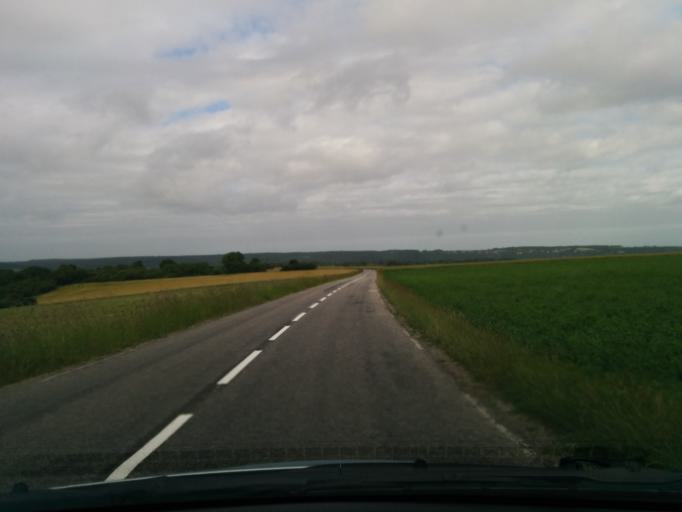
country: FR
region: Ile-de-France
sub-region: Departement des Yvelines
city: Buchelay
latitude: 49.0138
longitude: 1.6698
